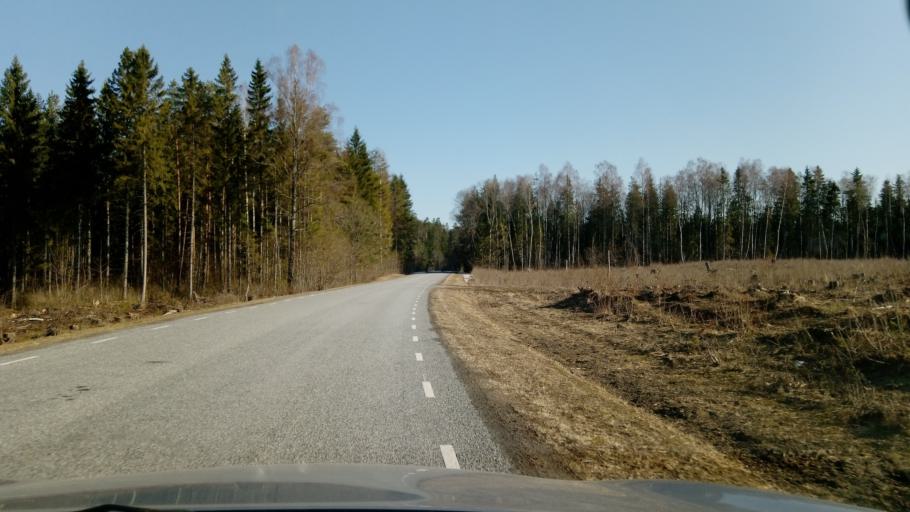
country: EE
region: Laeaene-Virumaa
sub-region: Tamsalu vald
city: Tamsalu
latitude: 59.2280
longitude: 26.1656
